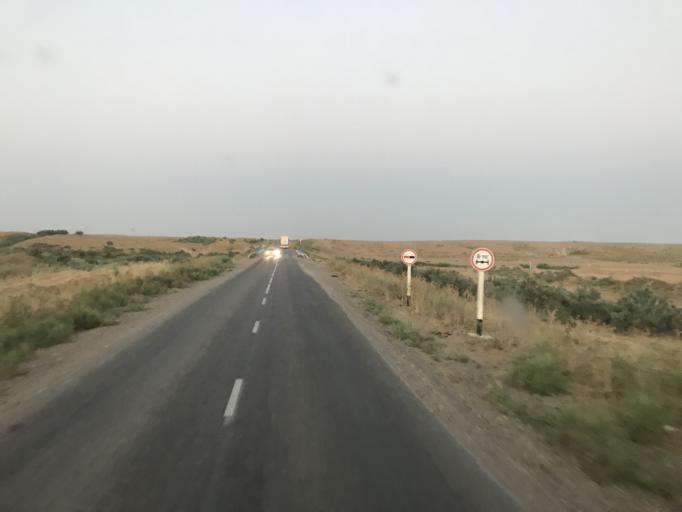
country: UZ
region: Toshkent
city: Chinoz
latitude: 41.1992
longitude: 68.6088
